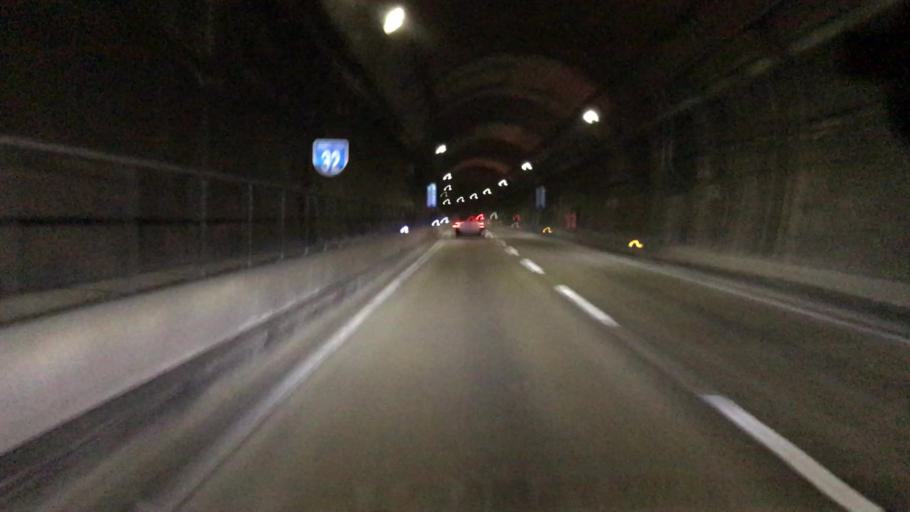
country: JP
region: Hyogo
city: Kobe
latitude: 34.7502
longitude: 135.1659
